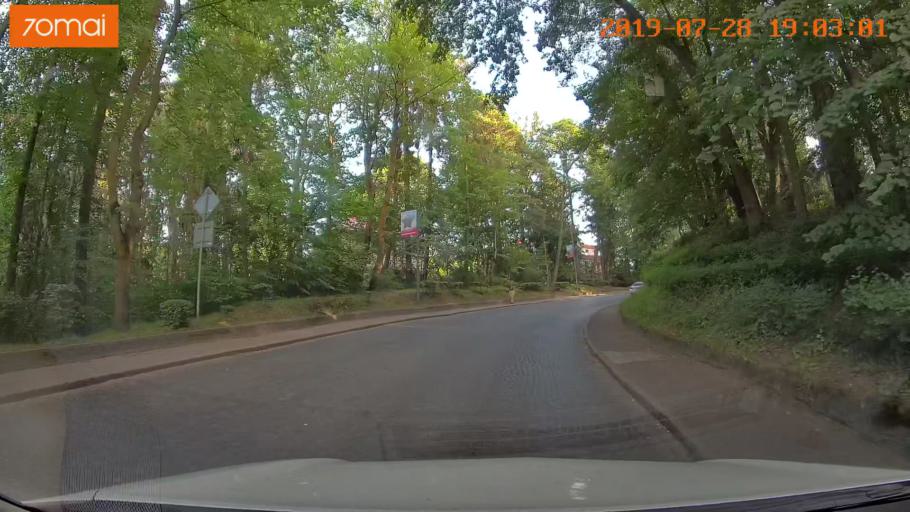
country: RU
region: Kaliningrad
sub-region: Gorod Svetlogorsk
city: Svetlogorsk
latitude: 54.9375
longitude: 20.1630
